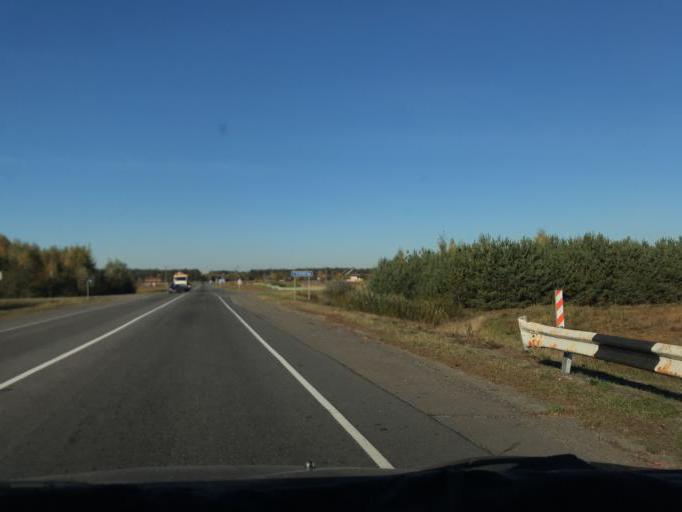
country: BY
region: Gomel
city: Kalinkavichy
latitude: 52.0791
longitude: 29.3611
